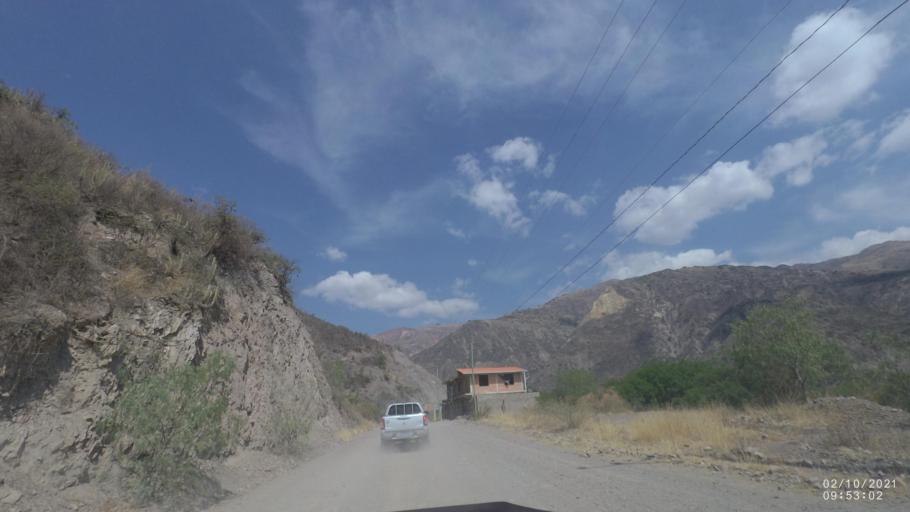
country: BO
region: Cochabamba
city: Irpa Irpa
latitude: -17.8011
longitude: -66.3469
